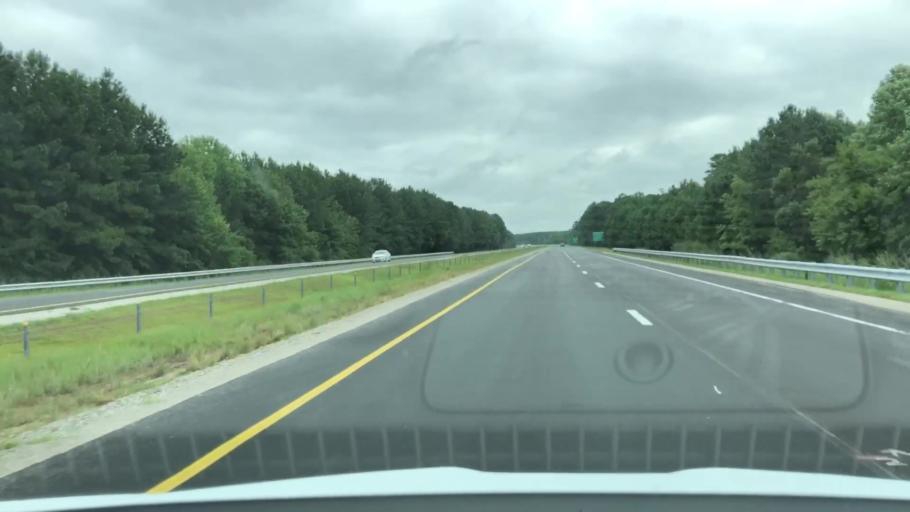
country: US
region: North Carolina
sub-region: Wilson County
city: Lucama
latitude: 35.6514
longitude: -77.9607
